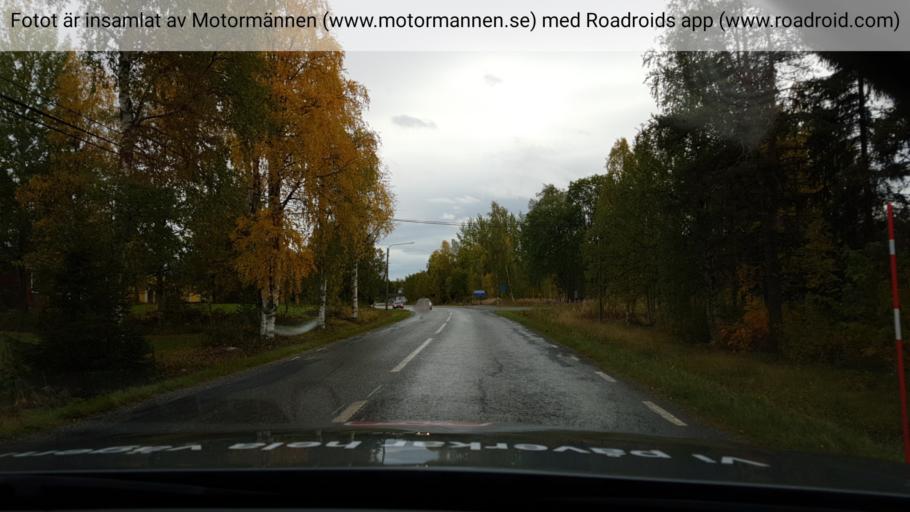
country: SE
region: Vaesterbotten
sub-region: Vilhelmina Kommun
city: Sjoberg
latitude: 64.6403
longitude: 16.3590
